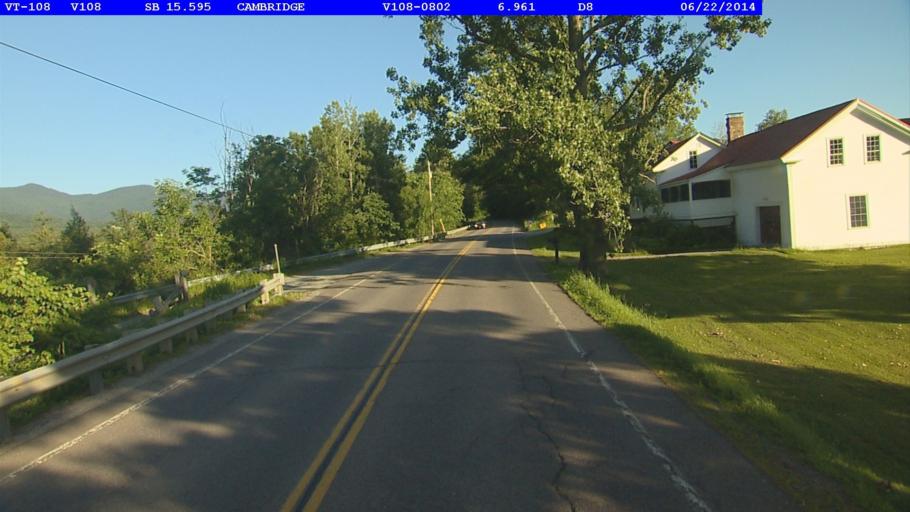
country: US
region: Vermont
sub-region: Lamoille County
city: Johnson
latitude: 44.6211
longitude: -72.8240
